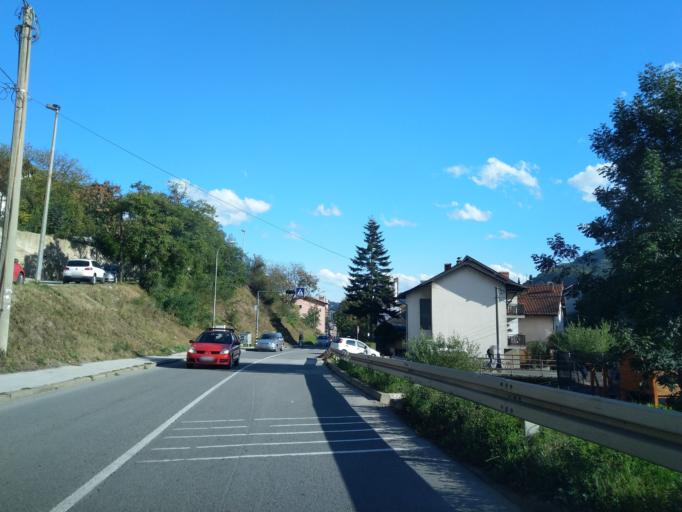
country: RS
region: Central Serbia
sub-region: Zlatiborski Okrug
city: Uzice
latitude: 43.8589
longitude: 19.8290
